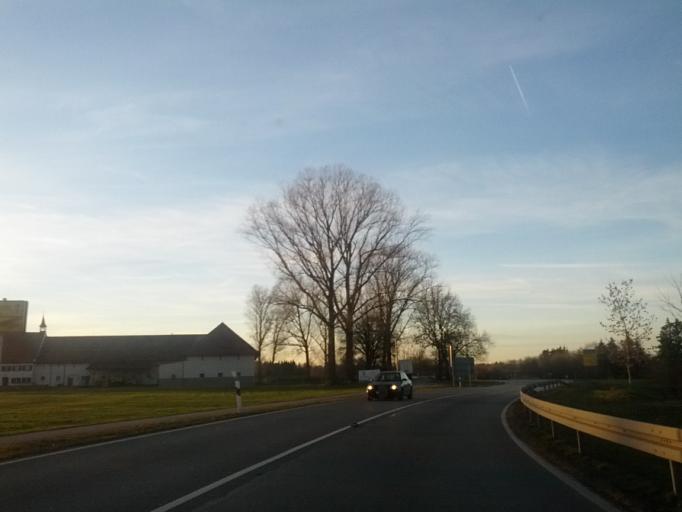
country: DE
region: Bavaria
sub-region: Swabia
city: Heimertingen
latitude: 48.0310
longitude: 10.1485
